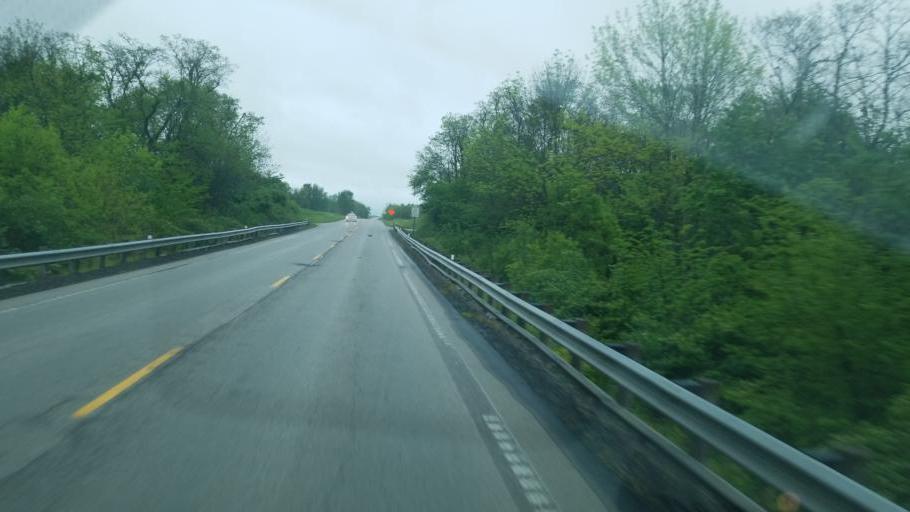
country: US
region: Ohio
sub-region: Highland County
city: Leesburg
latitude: 39.2975
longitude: -83.5850
